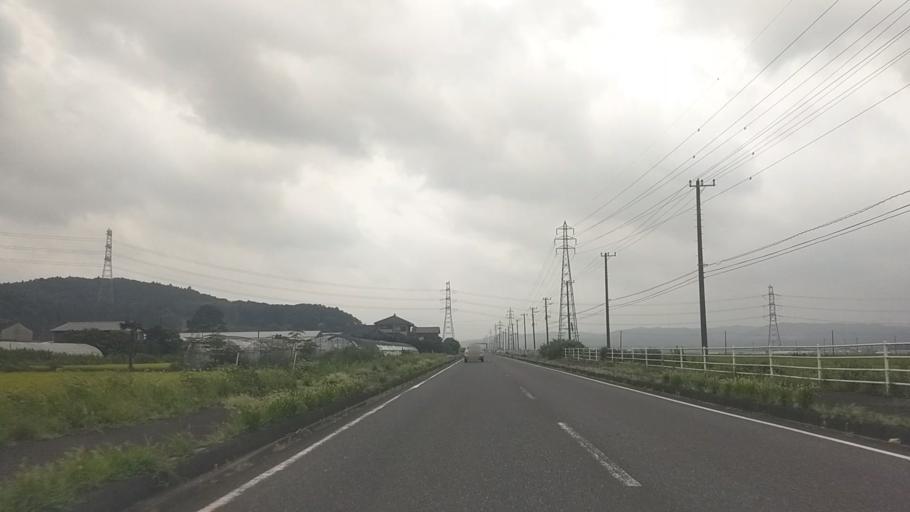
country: JP
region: Chiba
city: Kisarazu
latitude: 35.3493
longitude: 140.0548
